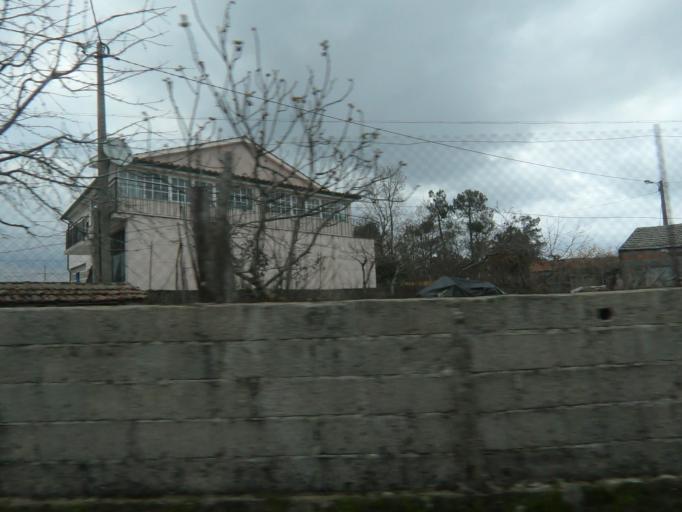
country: PT
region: Vila Real
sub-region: Sabrosa
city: Sabrosa
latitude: 41.3307
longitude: -7.6301
